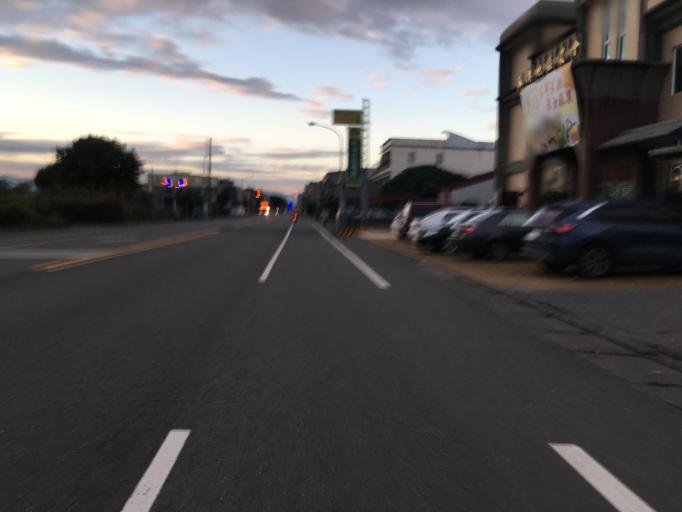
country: TW
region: Taiwan
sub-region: Yilan
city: Yilan
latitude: 24.6402
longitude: 121.8317
